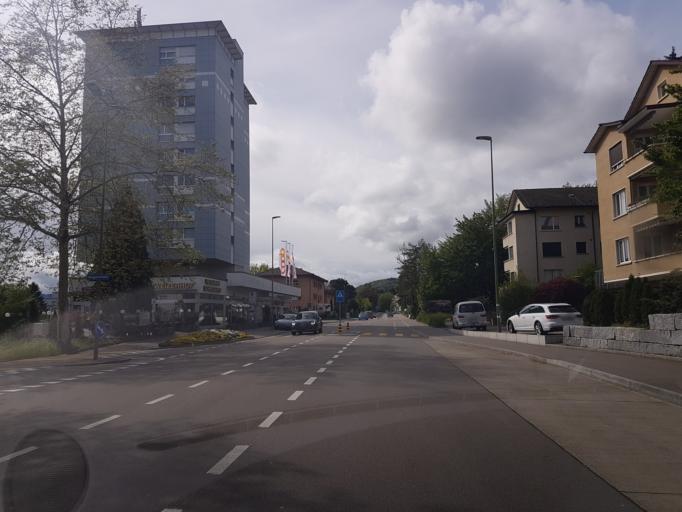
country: CH
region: Zurich
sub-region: Bezirk Dietikon
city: Oberengstringen / Sonnenberg
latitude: 47.4102
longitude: 8.4591
